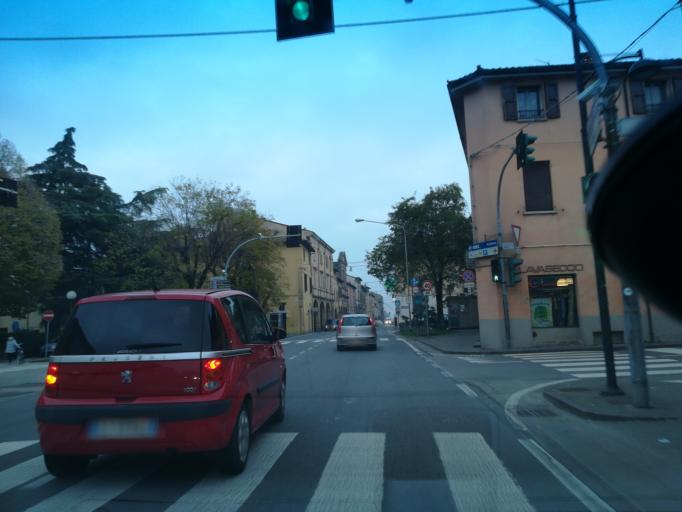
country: IT
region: Emilia-Romagna
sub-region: Provincia di Ravenna
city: Castel Bolognese
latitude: 44.3204
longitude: 11.7977
